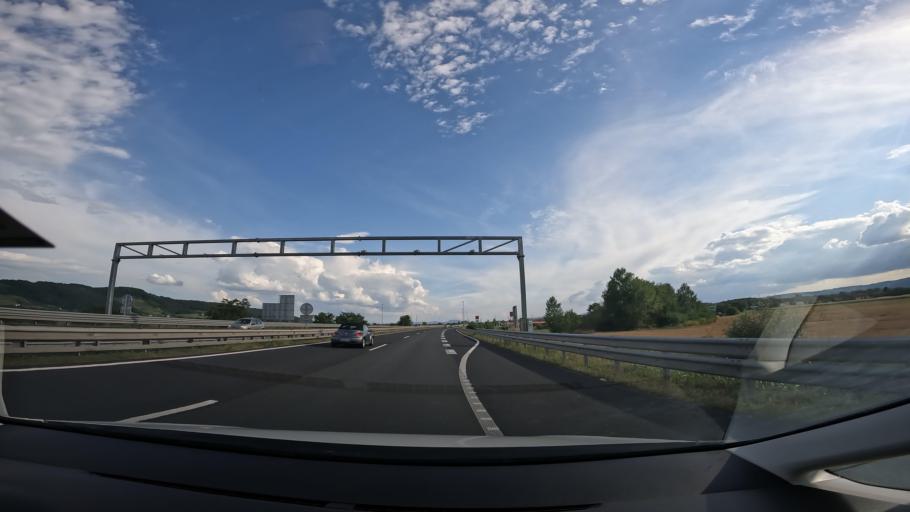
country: SI
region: Duplek
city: Zgornji Duplek
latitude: 46.5372
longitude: 15.7024
